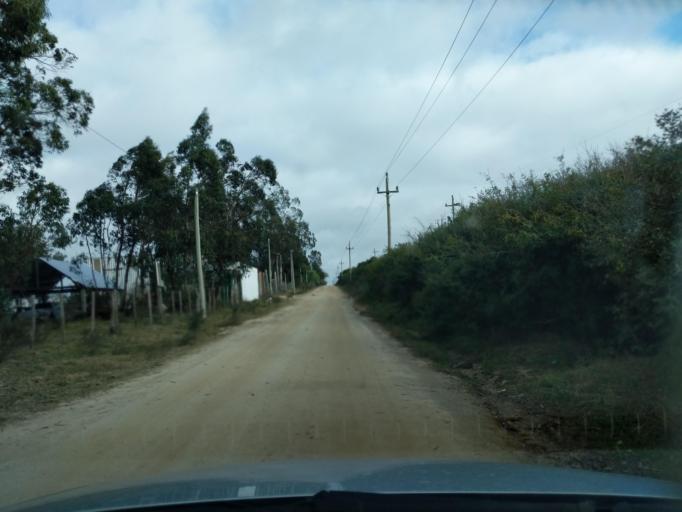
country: UY
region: Florida
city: Florida
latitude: -34.0589
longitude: -56.2162
